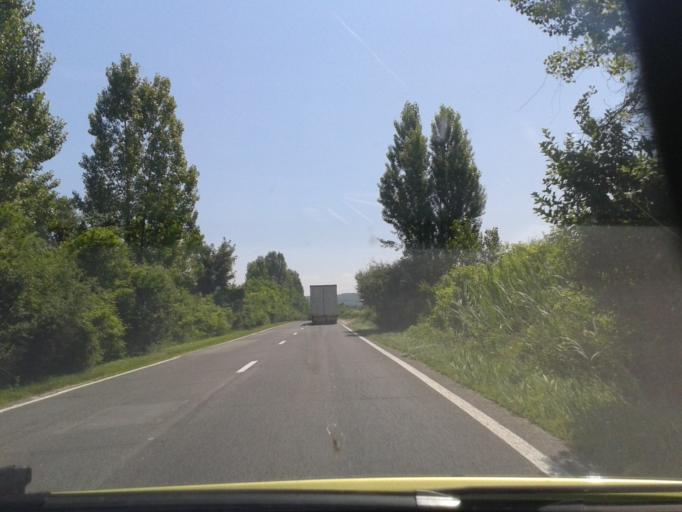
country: RO
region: Timis
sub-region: Comuna Margina
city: Margina
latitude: 45.8510
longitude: 22.2961
